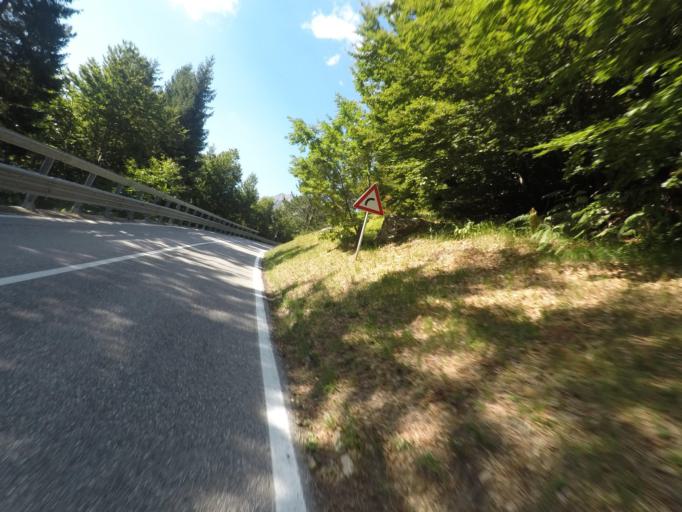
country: IT
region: Tuscany
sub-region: Provincia di Massa-Carrara
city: Comano
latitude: 44.2922
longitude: 10.2051
